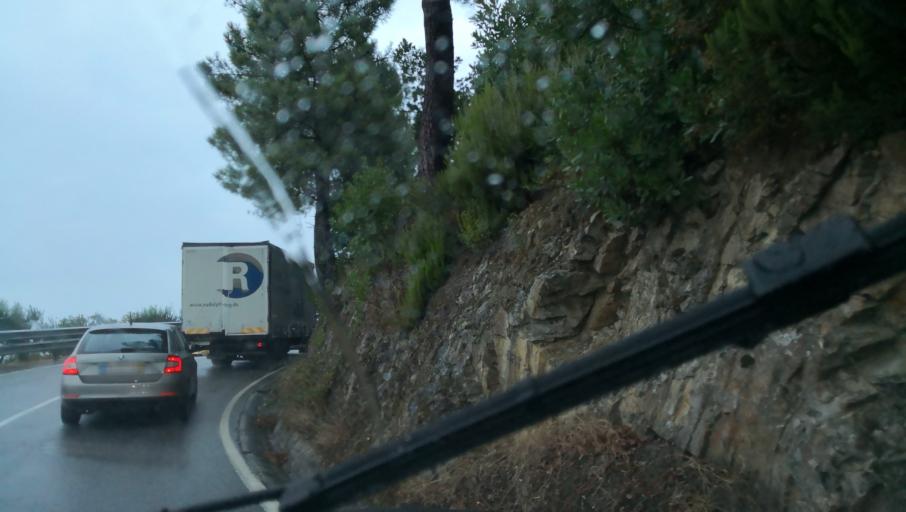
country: PT
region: Vila Real
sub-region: Vila Real
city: Vila Real
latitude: 41.2433
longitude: -7.7271
